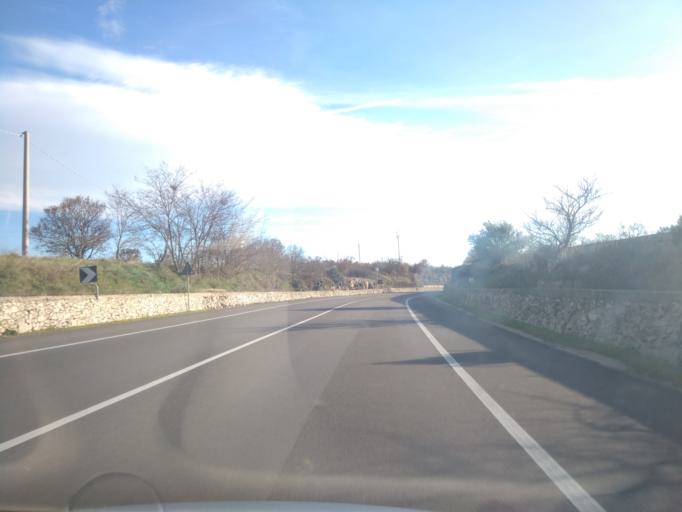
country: IT
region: Apulia
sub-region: Provincia di Bari
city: Gioia del Colle
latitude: 40.7428
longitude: 16.9724
